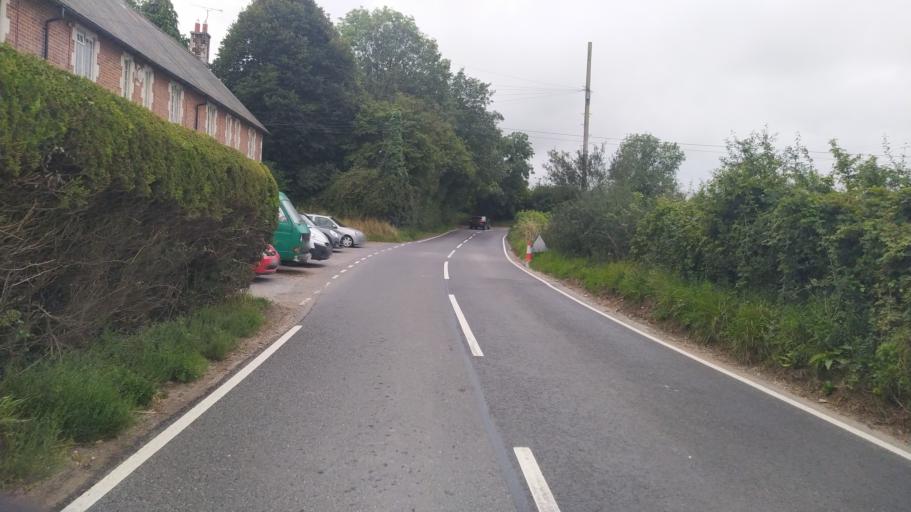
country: GB
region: England
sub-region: Dorset
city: Dorchester
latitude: 50.7553
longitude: -2.3652
